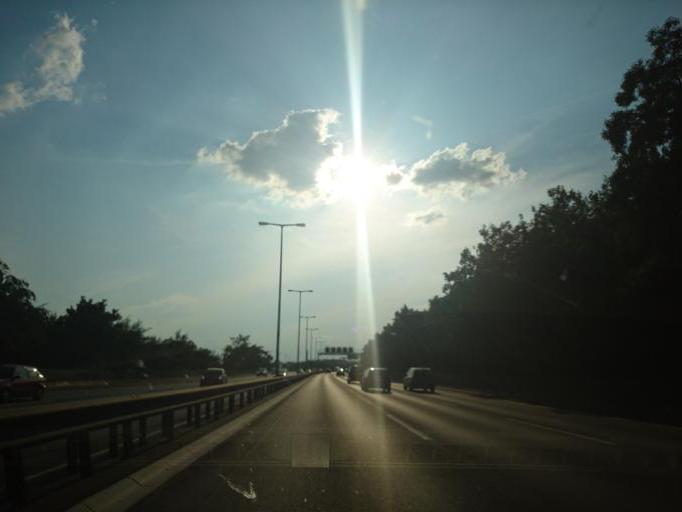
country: DE
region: Berlin
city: Friedenau
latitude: 52.4779
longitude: 13.3240
